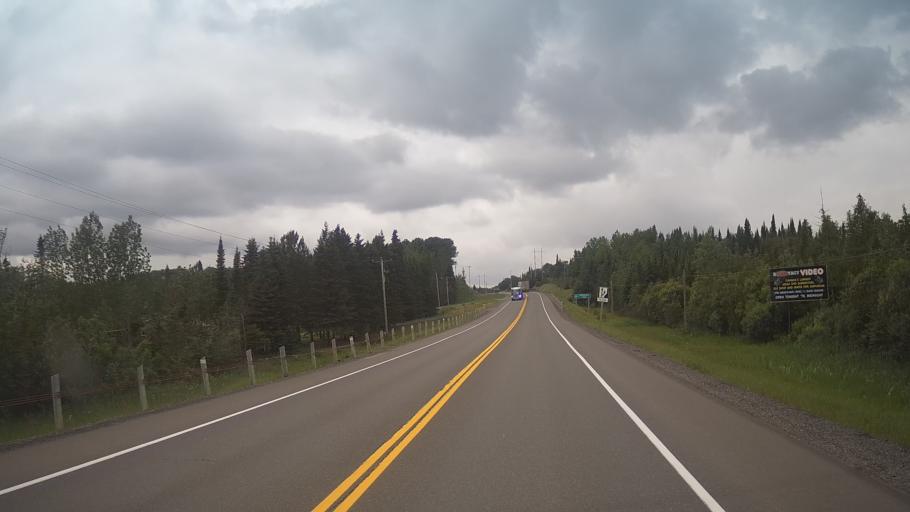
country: CA
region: Ontario
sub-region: Thunder Bay District
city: Thunder Bay
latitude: 48.5118
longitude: -89.4768
